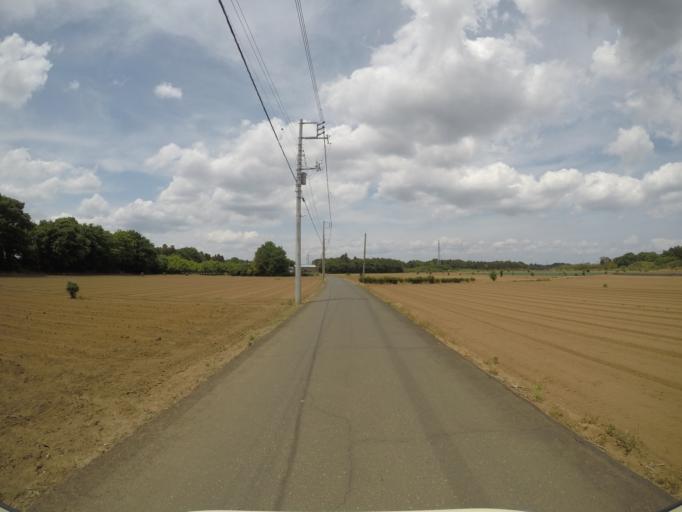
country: JP
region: Ibaraki
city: Ushiku
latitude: 35.9789
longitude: 140.1166
